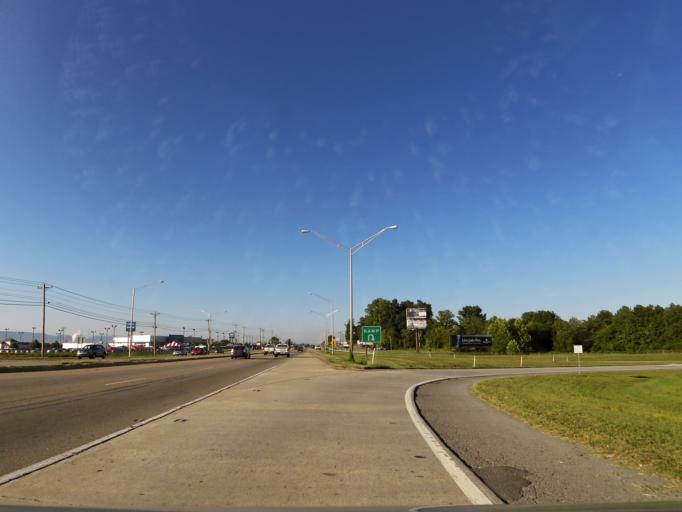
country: US
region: Tennessee
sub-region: Blount County
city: Alcoa
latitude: 35.8355
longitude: -83.9714
